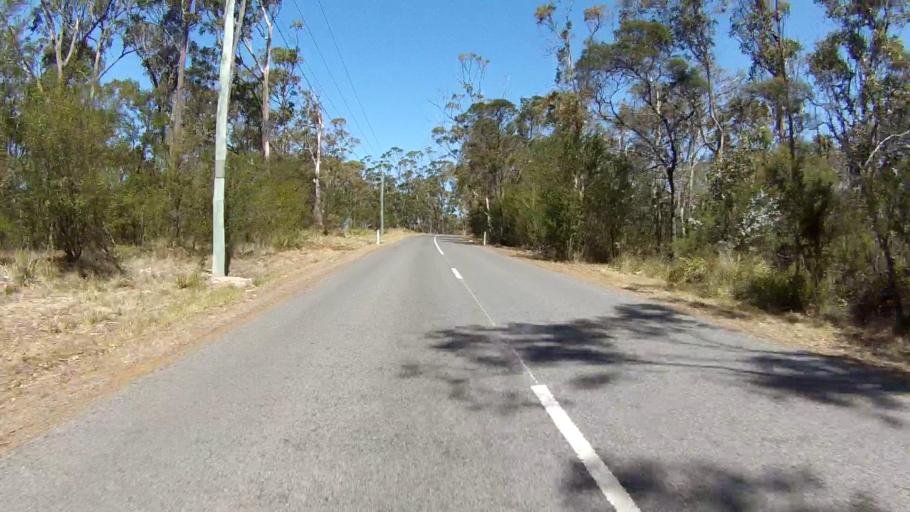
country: AU
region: Tasmania
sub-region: Clarence
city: Sandford
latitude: -43.0156
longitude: 147.4815
